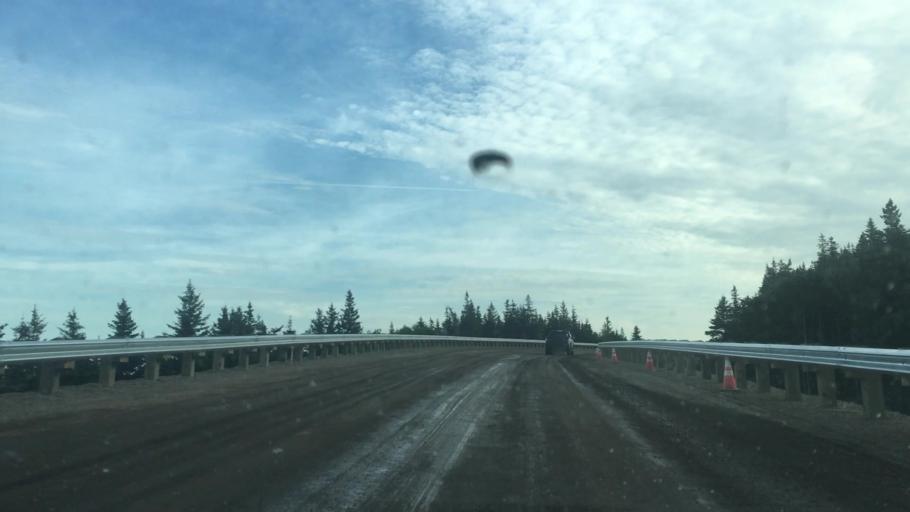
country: CA
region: Nova Scotia
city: Sydney Mines
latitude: 46.8100
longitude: -60.8419
